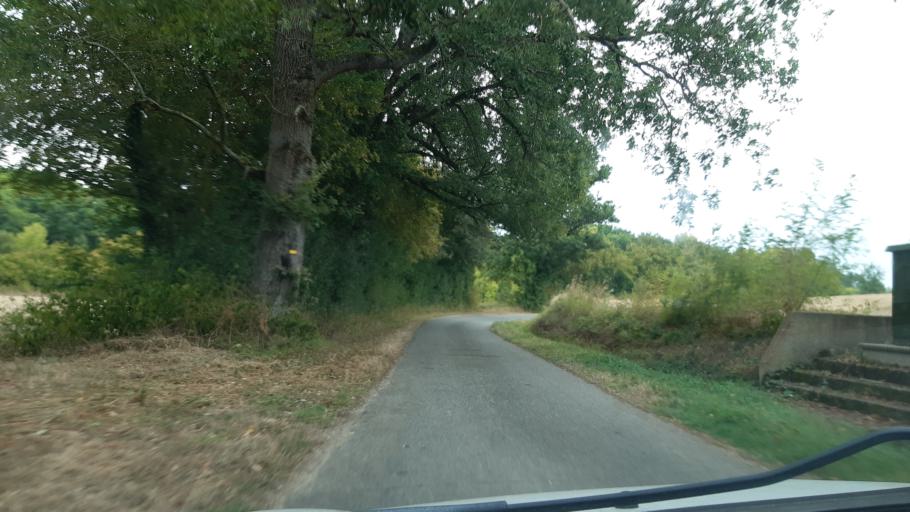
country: FR
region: Midi-Pyrenees
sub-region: Departement du Gers
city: Gimont
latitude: 43.6924
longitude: 0.9718
